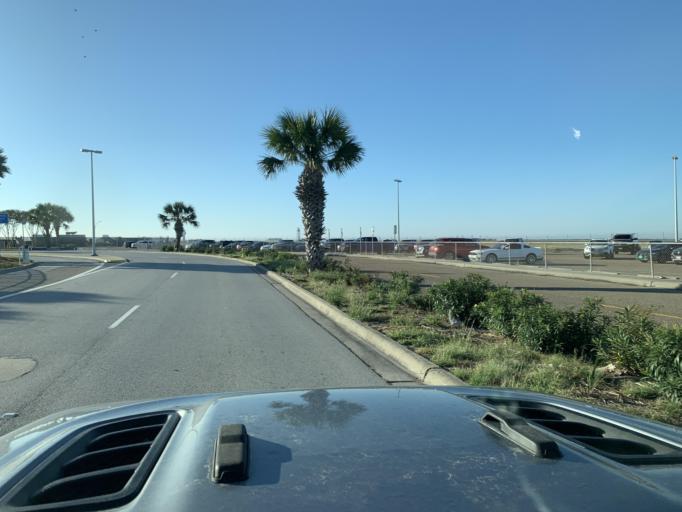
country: US
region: Texas
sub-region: Nueces County
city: Corpus Christi
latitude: 27.7755
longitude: -97.5041
